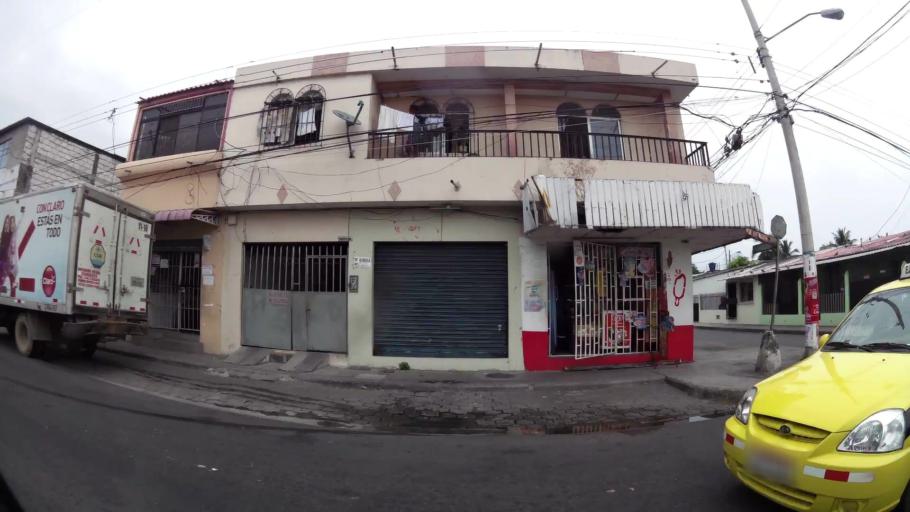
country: EC
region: Guayas
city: Eloy Alfaro
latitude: -2.1352
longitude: -79.8971
